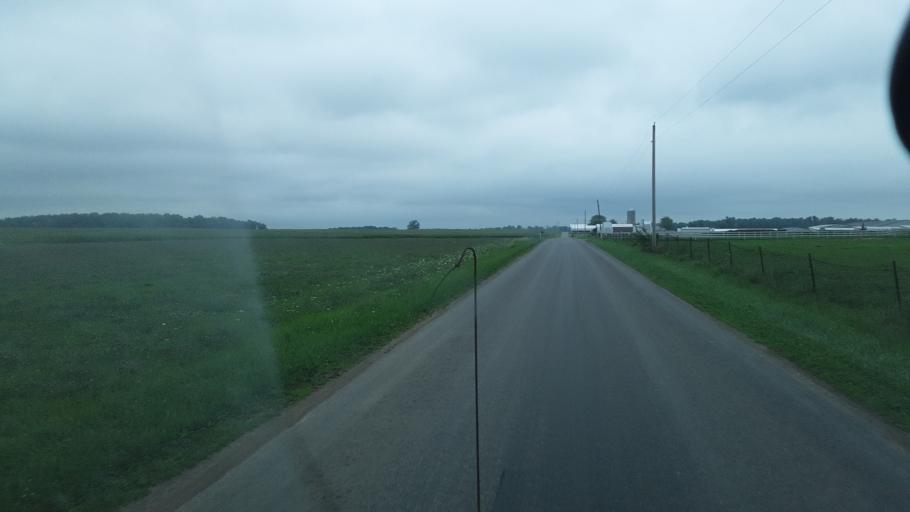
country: US
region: Indiana
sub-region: Adams County
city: Geneva
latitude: 40.6130
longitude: -84.9924
